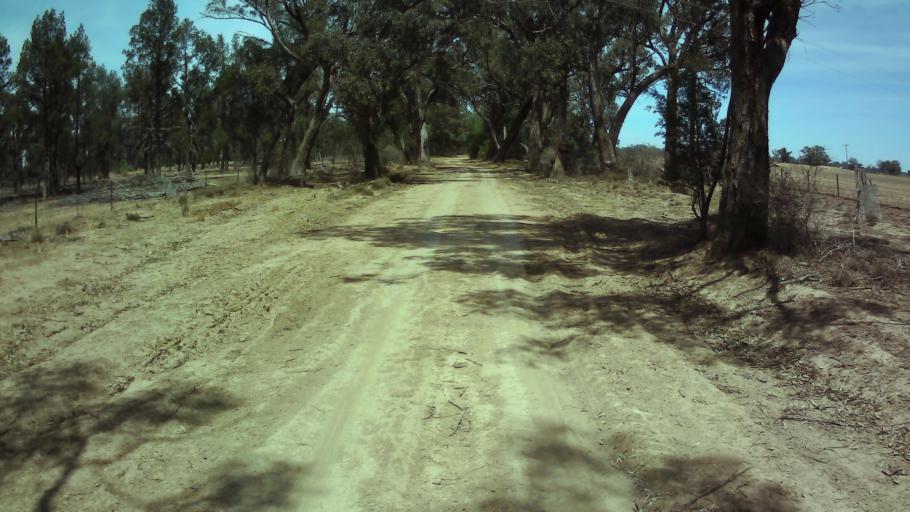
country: AU
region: New South Wales
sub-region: Weddin
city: Grenfell
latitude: -34.0303
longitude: 147.9356
